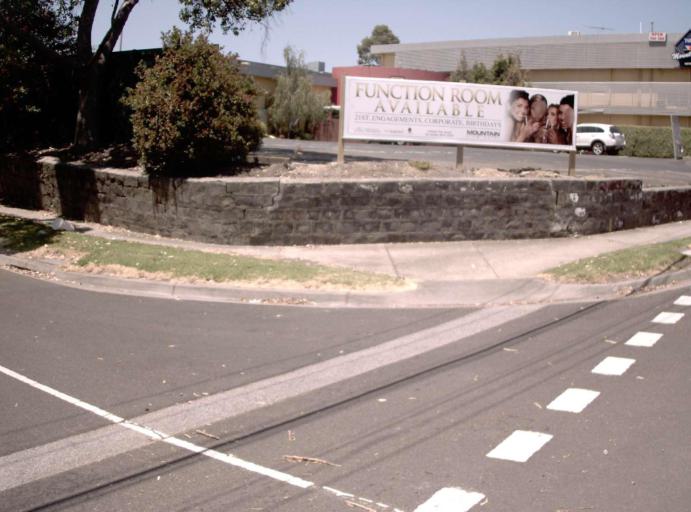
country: AU
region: Victoria
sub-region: Whitehorse
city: Vermont South
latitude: -37.8735
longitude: 145.1672
